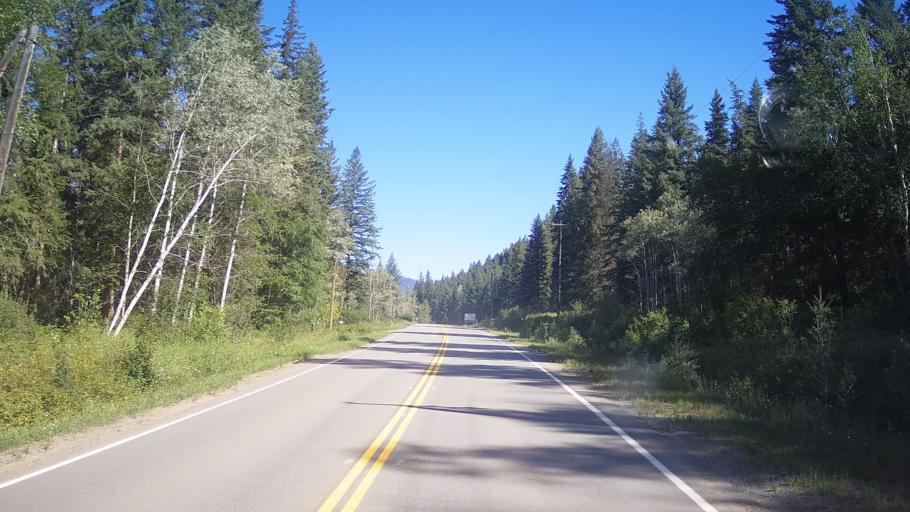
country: CA
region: British Columbia
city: Kamloops
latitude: 51.4475
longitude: -120.2127
